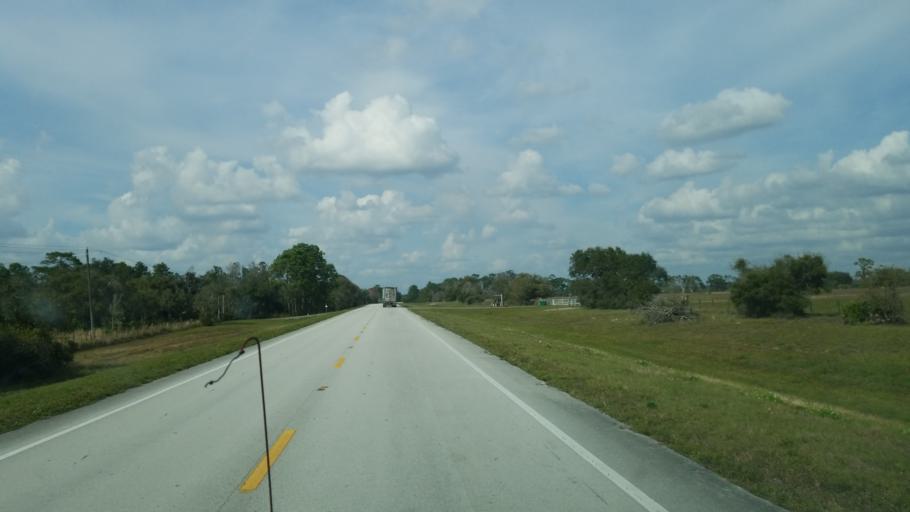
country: US
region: Florida
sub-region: Indian River County
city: Fellsmere
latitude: 27.7138
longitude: -80.9116
